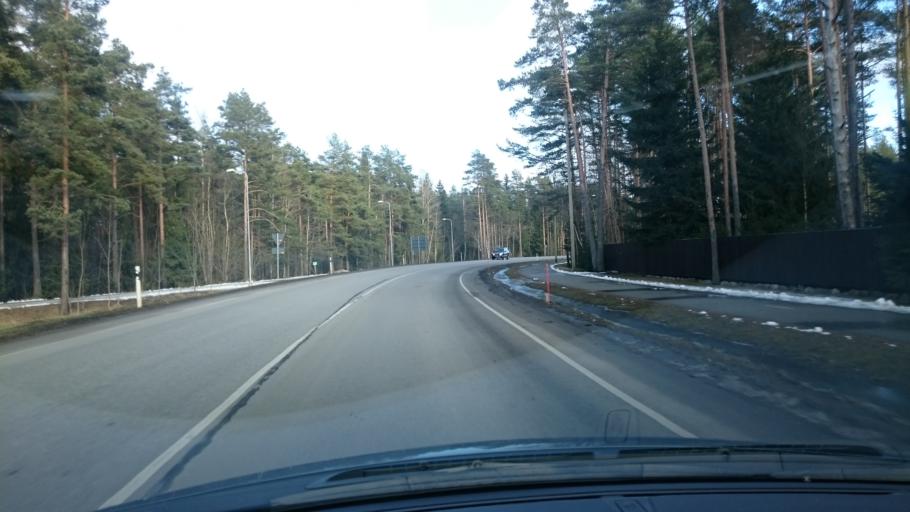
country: EE
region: Harju
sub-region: Kiili vald
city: Kiili
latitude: 59.3541
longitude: 24.7748
